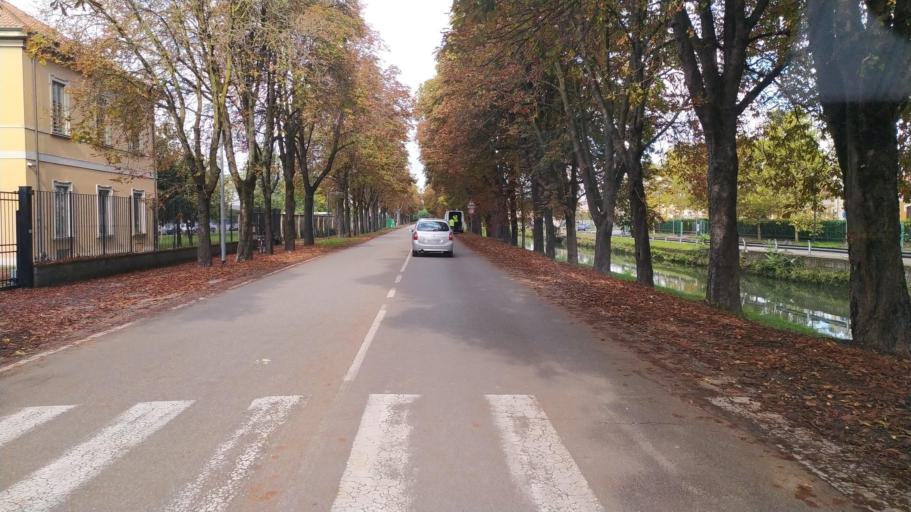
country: IT
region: Lombardy
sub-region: Provincia di Pavia
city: Pavia
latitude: 45.2027
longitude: 9.1532
